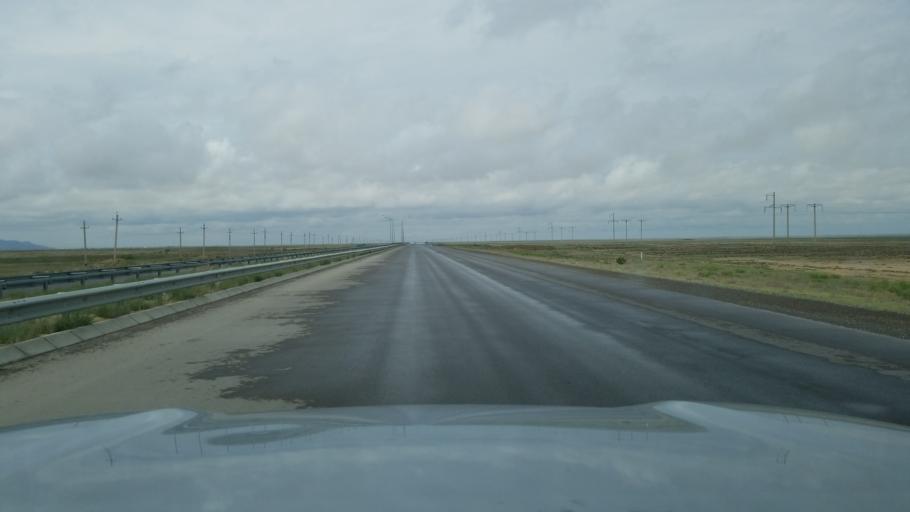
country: TM
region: Balkan
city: Gazanjyk
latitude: 39.1924
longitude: 55.7836
